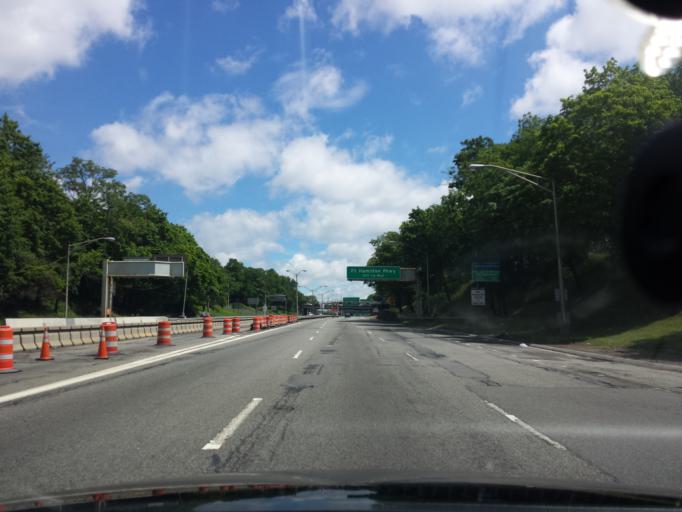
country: US
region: New York
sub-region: Kings County
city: Bensonhurst
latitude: 40.6169
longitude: -74.0255
